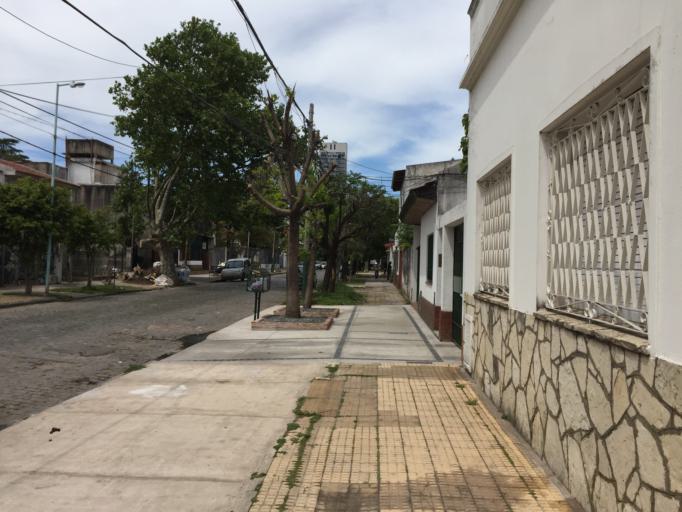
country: AR
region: Buenos Aires
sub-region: Partido de Lomas de Zamora
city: Lomas de Zamora
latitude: -34.7393
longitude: -58.3911
